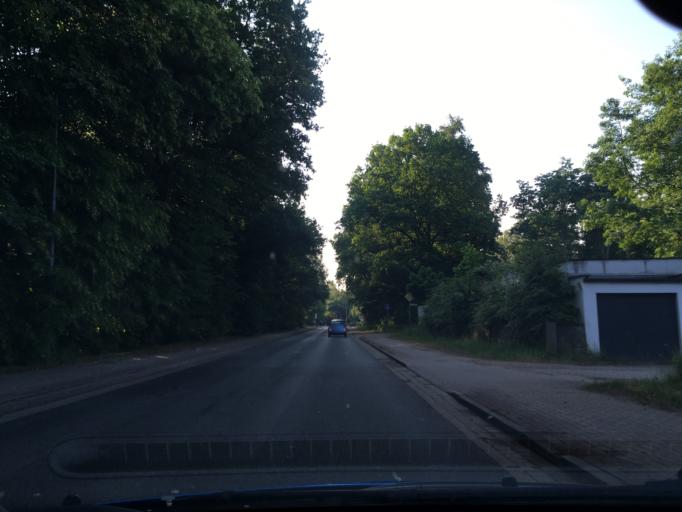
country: DE
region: Lower Saxony
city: Buchholz in der Nordheide
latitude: 53.3395
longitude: 9.8581
